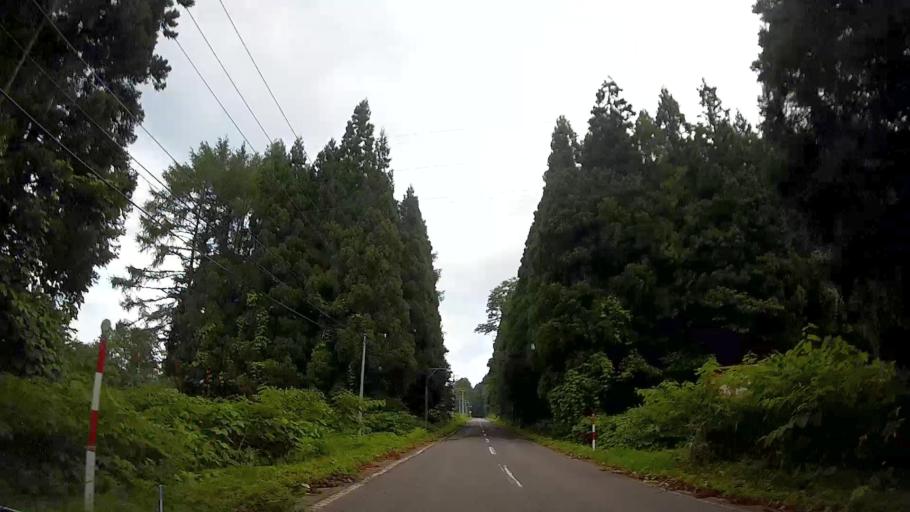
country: JP
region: Hokkaido
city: Nanae
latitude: 42.0915
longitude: 140.5561
